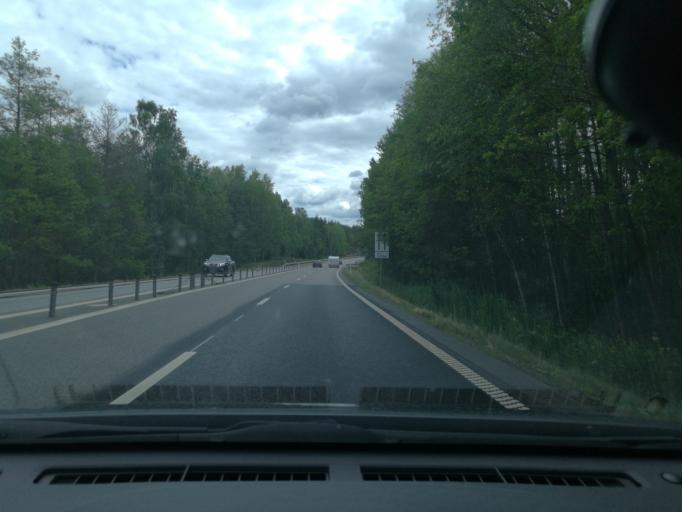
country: SE
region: OEstergoetland
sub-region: Valdemarsviks Kommun
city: Valdemarsvik
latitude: 58.1102
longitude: 16.5428
